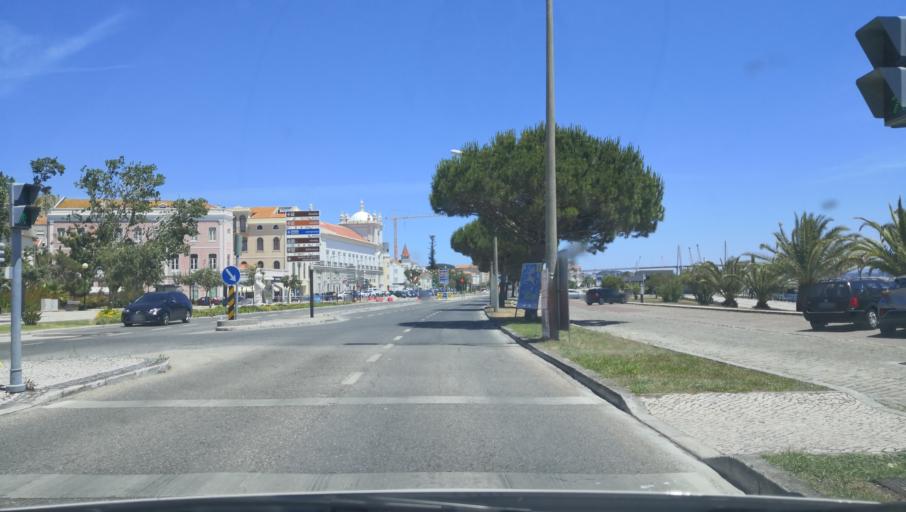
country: PT
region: Coimbra
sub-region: Figueira da Foz
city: Figueira da Foz
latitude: 40.1483
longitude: -8.8615
